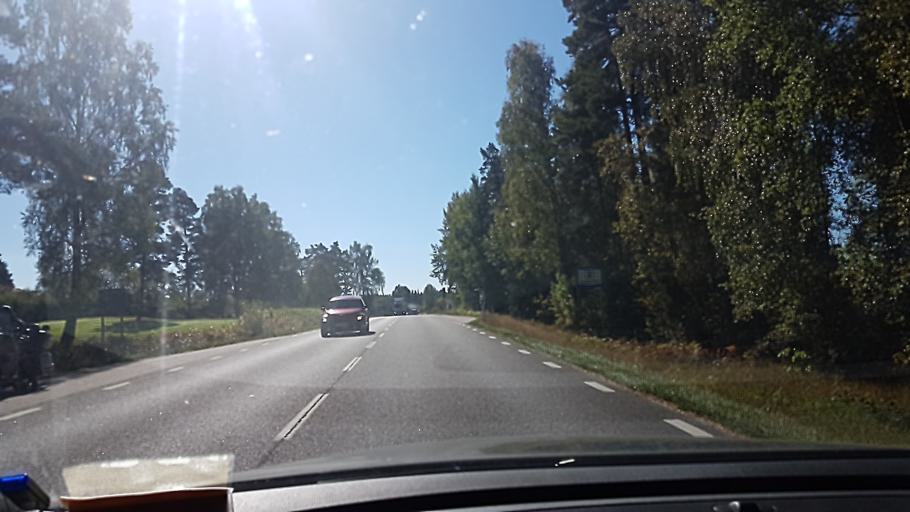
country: SE
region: Kronoberg
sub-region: Lessebo Kommun
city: Lessebo
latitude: 56.7639
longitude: 15.2645
